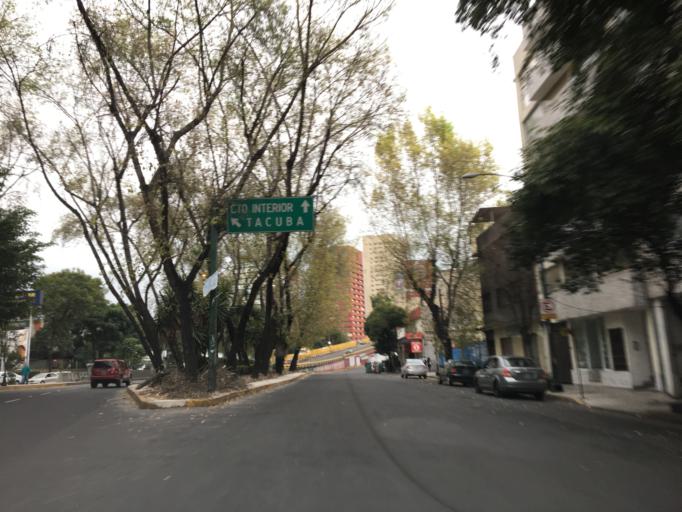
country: MX
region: Mexico City
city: Cuauhtemoc
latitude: 19.4357
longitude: -99.1669
